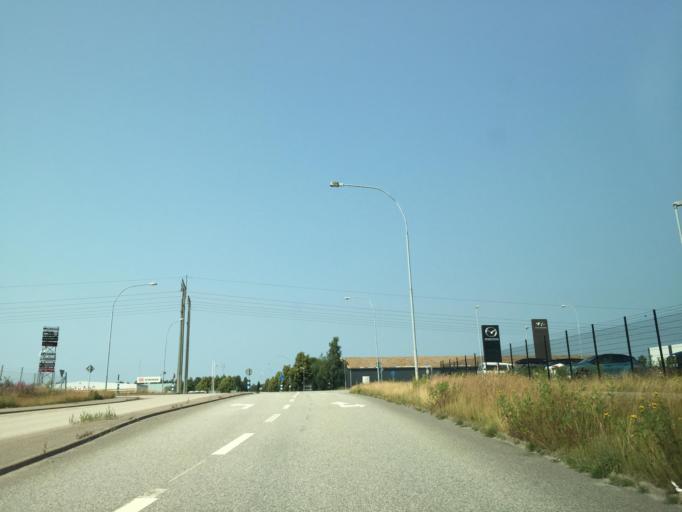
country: SE
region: Vaestra Goetaland
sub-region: Trollhattan
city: Trollhattan
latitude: 58.3395
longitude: 12.2542
